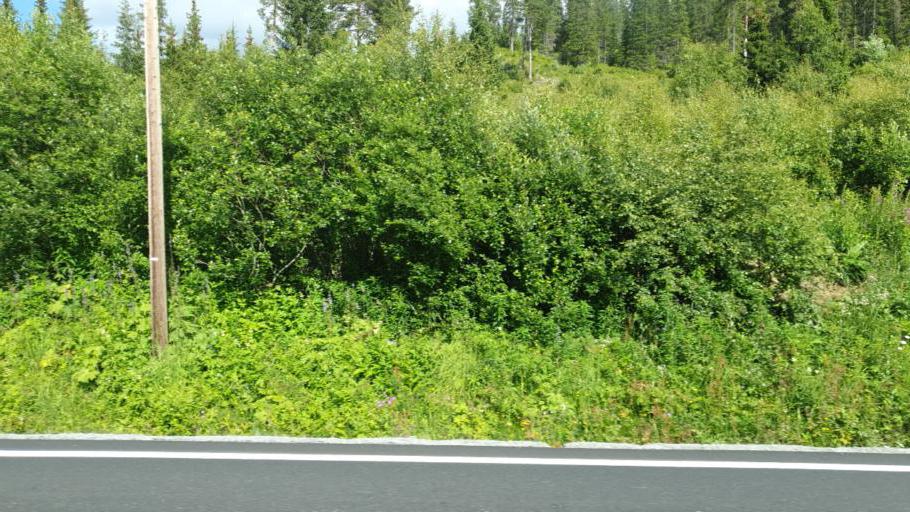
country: NO
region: Oppland
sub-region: Oystre Slidre
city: Heggenes
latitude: 61.1712
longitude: 8.9946
